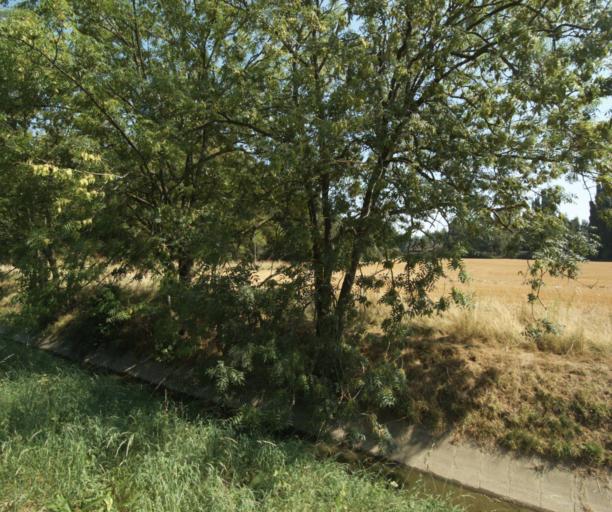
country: FR
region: Nord-Pas-de-Calais
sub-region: Departement du Nord
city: Comines
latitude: 50.7561
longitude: 3.0294
